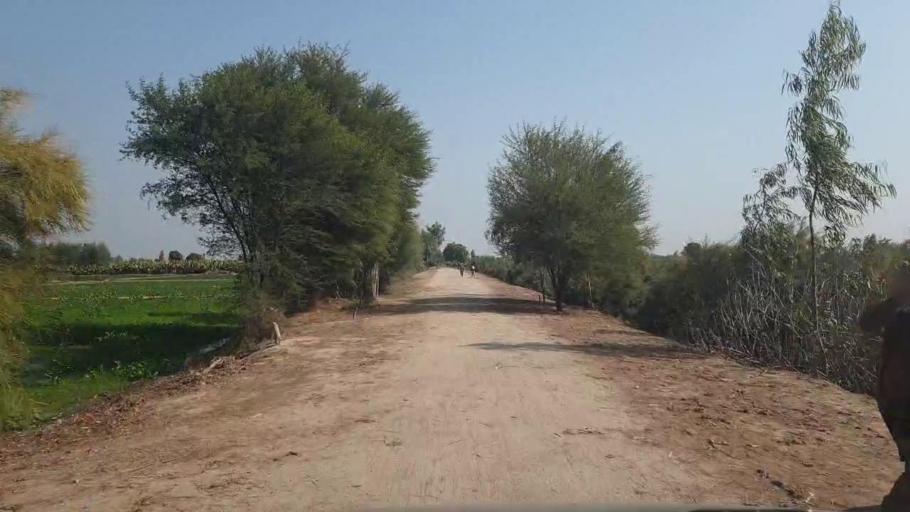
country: PK
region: Sindh
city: Tando Adam
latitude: 25.7985
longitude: 68.6239
